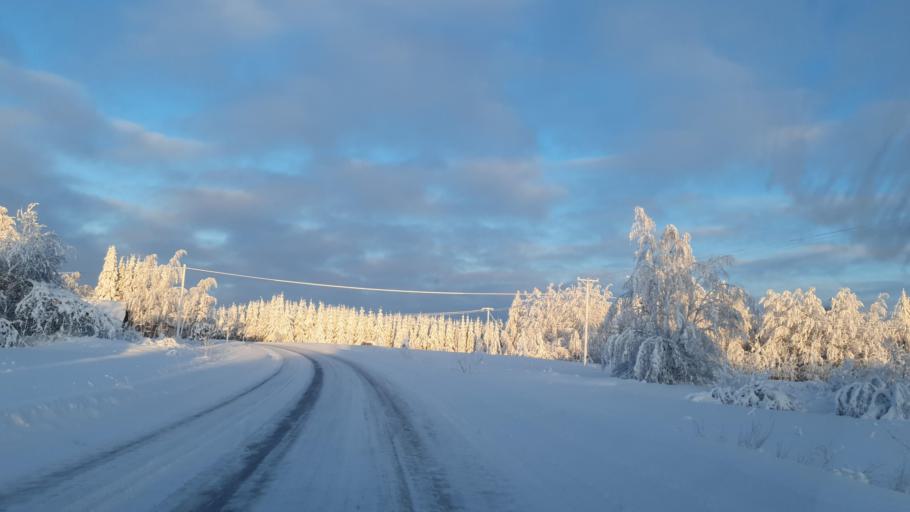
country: FI
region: Kainuu
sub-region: Kajaani
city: Vuokatti
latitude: 64.2643
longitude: 28.2435
